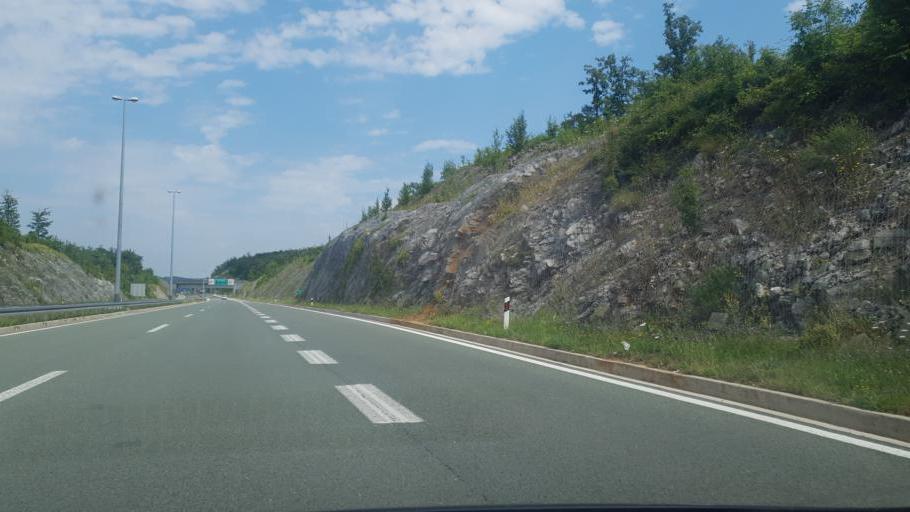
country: HR
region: Primorsko-Goranska
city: Matulji
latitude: 45.4453
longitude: 14.2735
